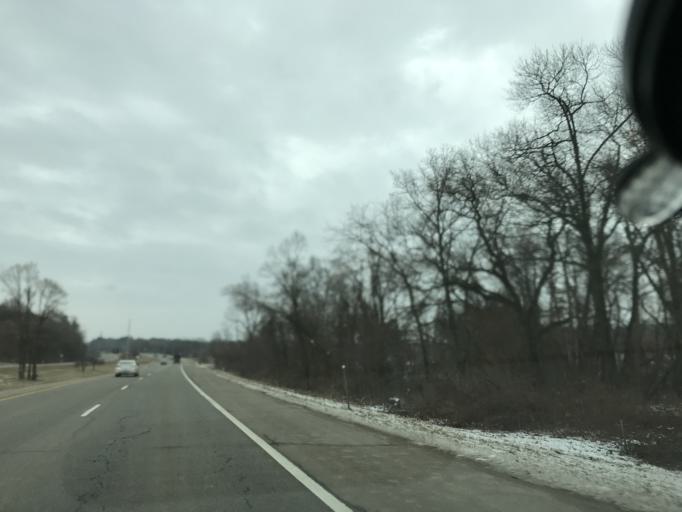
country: US
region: Michigan
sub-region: Kent County
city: Forest Hills
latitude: 42.9632
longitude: -85.5512
